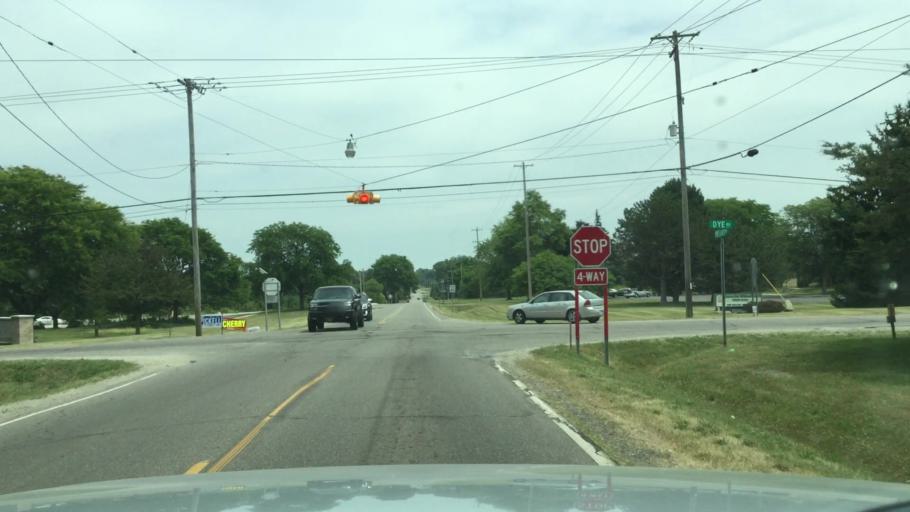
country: US
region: Michigan
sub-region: Genesee County
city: Swartz Creek
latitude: 43.0165
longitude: -83.7834
